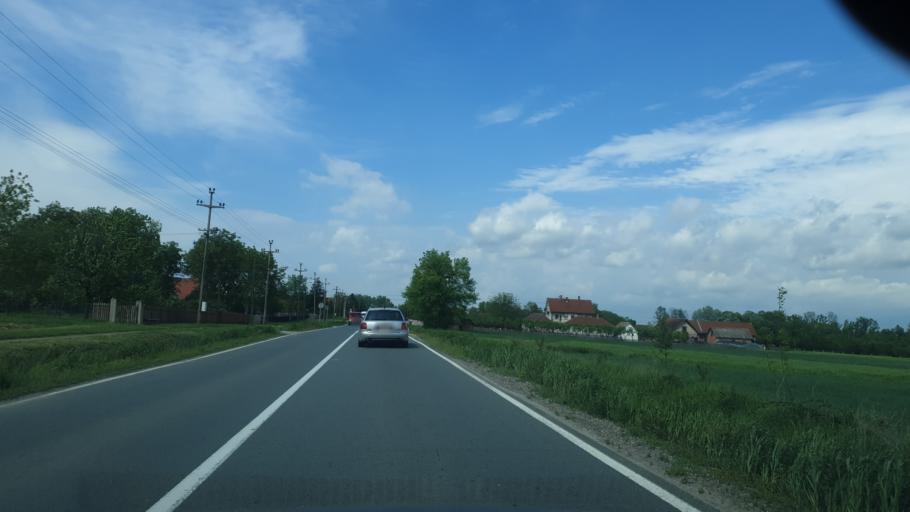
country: RS
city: Stubline
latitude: 44.5997
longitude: 20.1476
